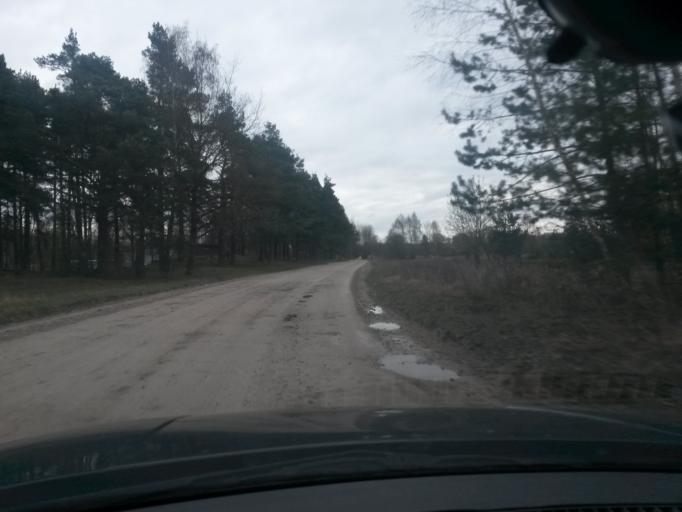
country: LV
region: Stopini
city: Ulbroka
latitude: 56.8926
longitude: 24.2440
